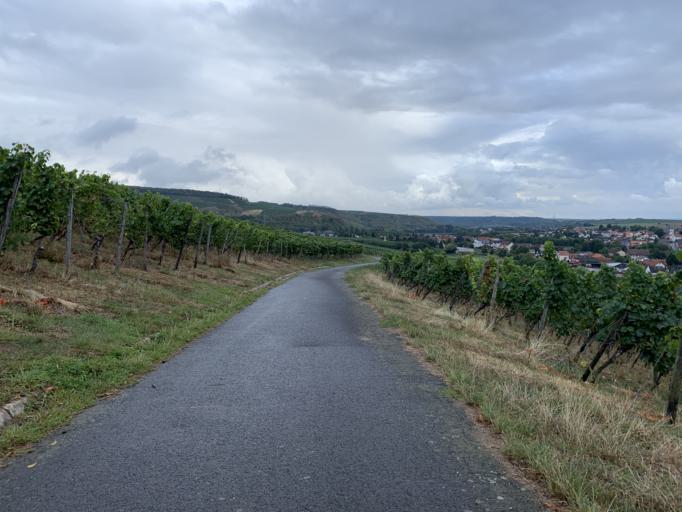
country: DE
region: Rheinland-Pfalz
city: Schweppenhausen
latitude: 49.9134
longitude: 7.8076
